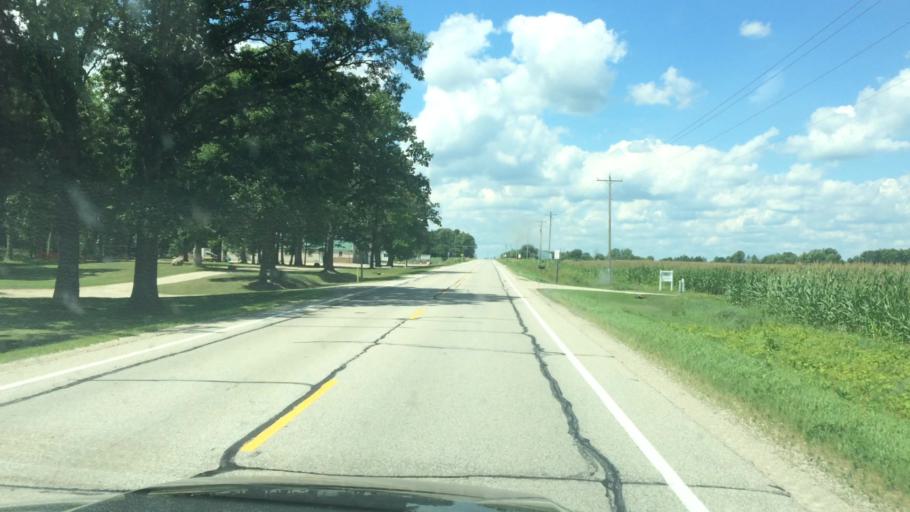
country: US
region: Wisconsin
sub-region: Marinette County
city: Peshtigo
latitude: 45.1081
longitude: -87.9649
